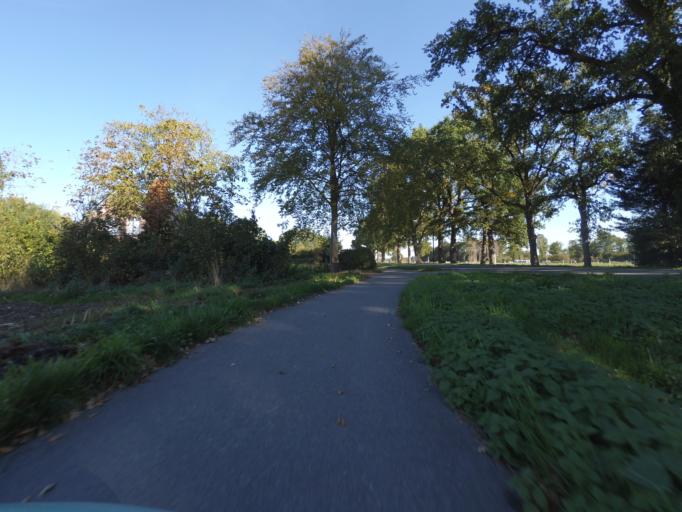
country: DE
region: North Rhine-Westphalia
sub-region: Regierungsbezirk Dusseldorf
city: Bocholt
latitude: 51.8866
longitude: 6.6325
